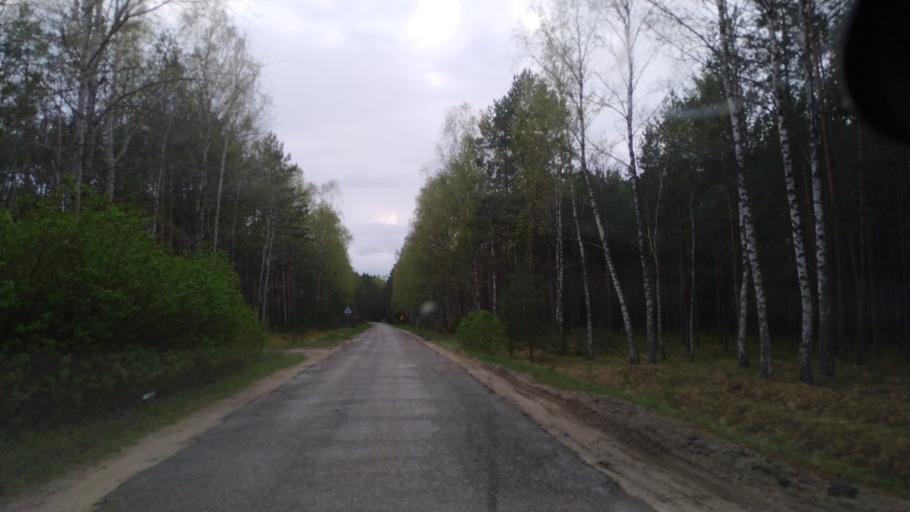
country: PL
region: Pomeranian Voivodeship
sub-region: Powiat starogardzki
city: Osiek
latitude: 53.6887
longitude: 18.5160
